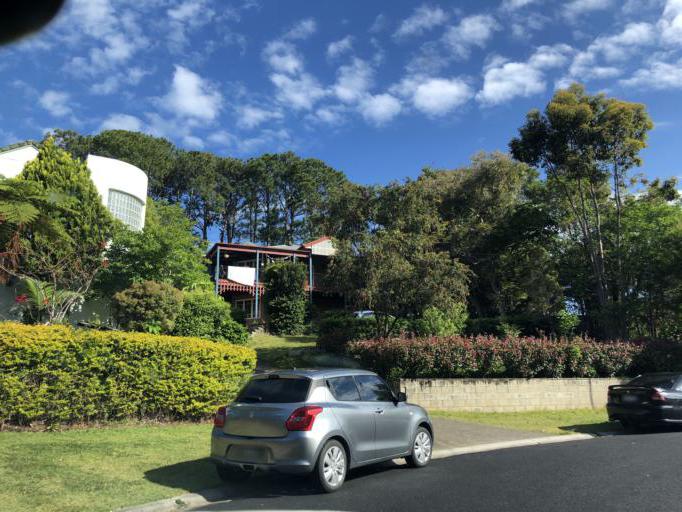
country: AU
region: New South Wales
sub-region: Coffs Harbour
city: Coffs Harbour
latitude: -30.2556
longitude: 153.1328
